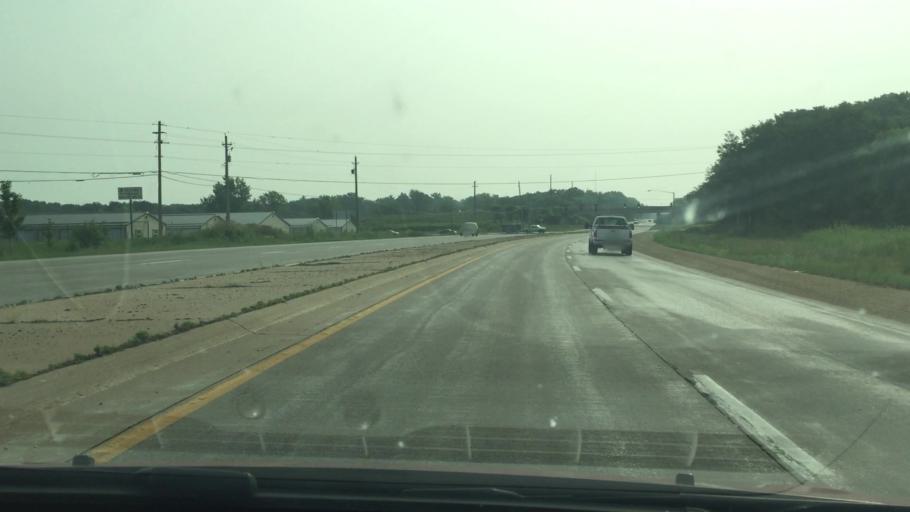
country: US
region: Iowa
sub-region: Scott County
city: Buffalo
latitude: 41.5089
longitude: -90.6771
